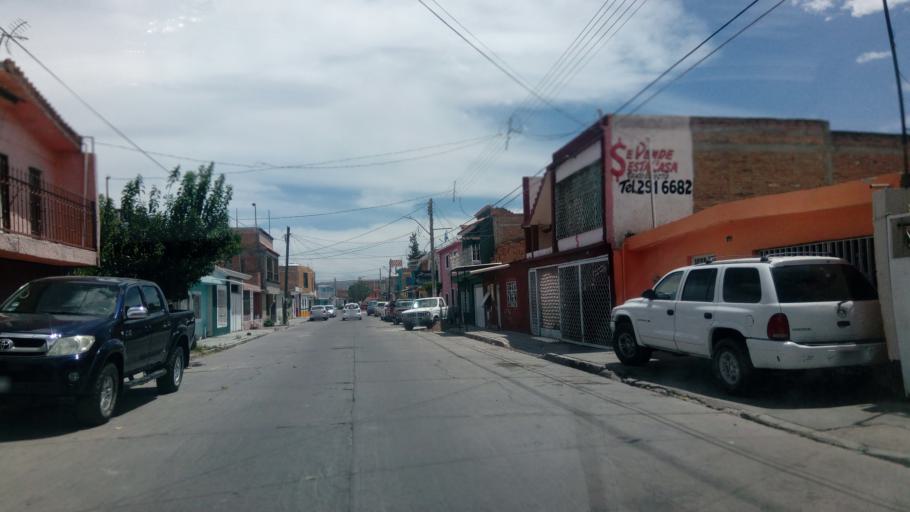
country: MX
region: Durango
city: Victoria de Durango
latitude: 24.0019
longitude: -104.6774
